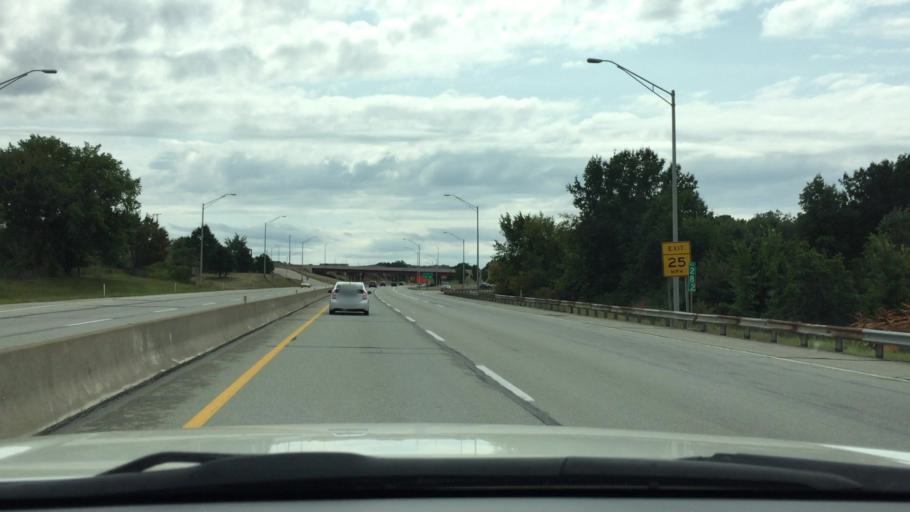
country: US
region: Pennsylvania
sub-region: Butler County
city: Cranberry Township
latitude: 40.6826
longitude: -80.1065
